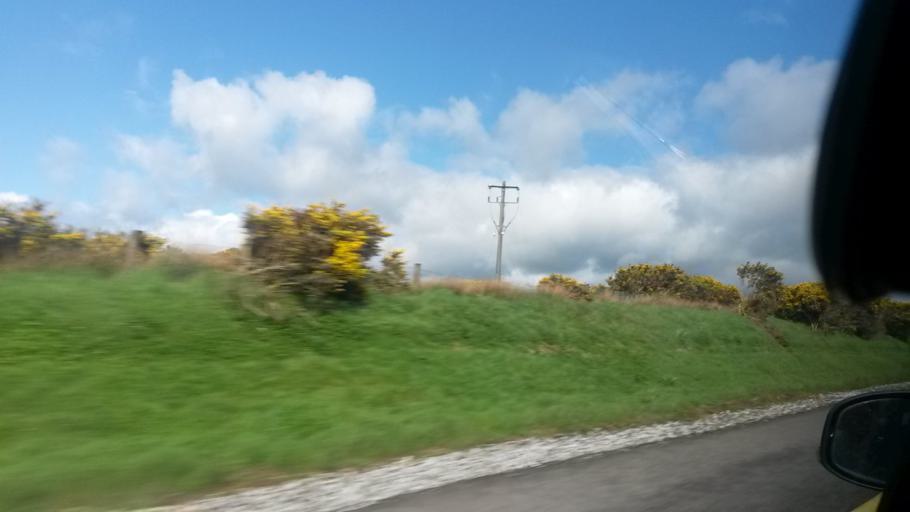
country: IE
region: Munster
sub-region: County Cork
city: Mitchelstown
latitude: 52.2097
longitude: -8.2759
